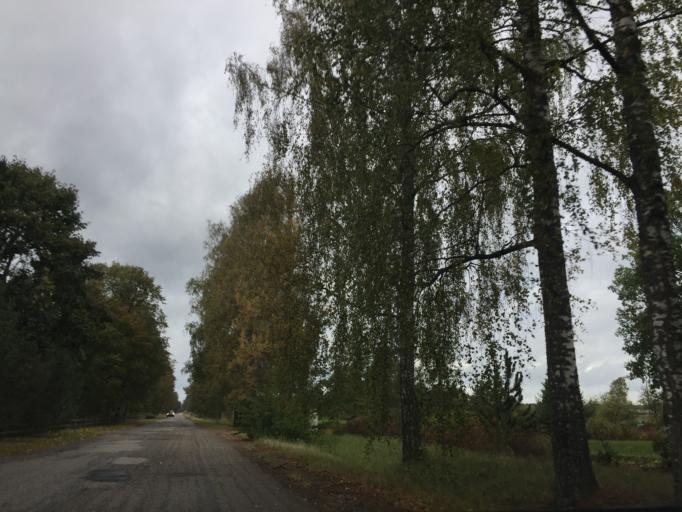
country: LV
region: Olaine
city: Olaine
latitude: 56.7661
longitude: 23.8825
